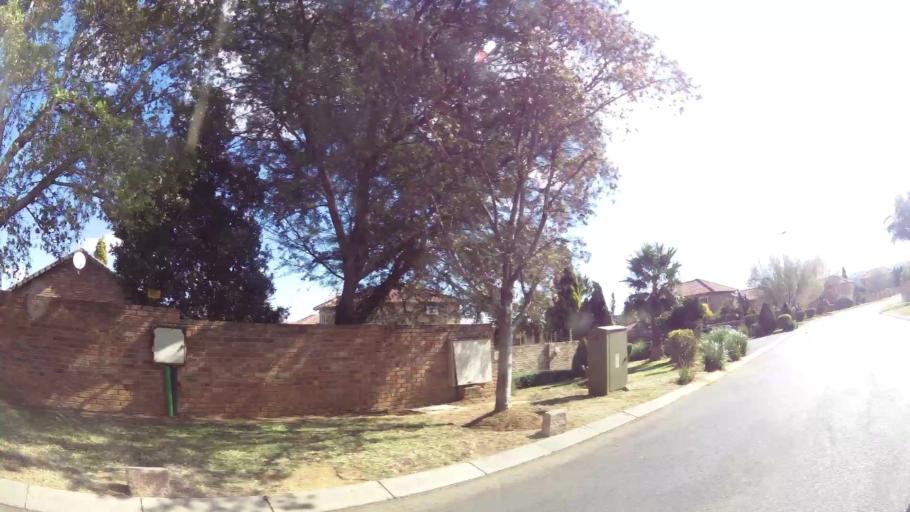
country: ZA
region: Gauteng
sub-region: City of Johannesburg Metropolitan Municipality
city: Midrand
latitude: -25.9949
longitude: 28.0992
